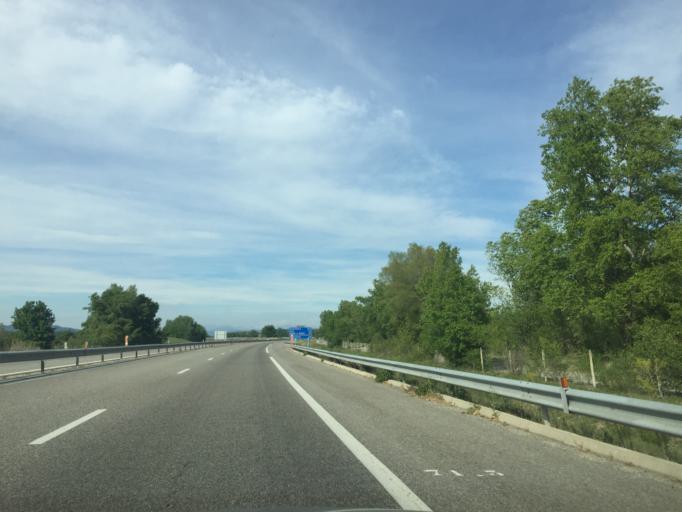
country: FR
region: Provence-Alpes-Cote d'Azur
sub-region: Departement des Alpes-de-Haute-Provence
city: Manosque
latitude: 43.8142
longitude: 5.8212
